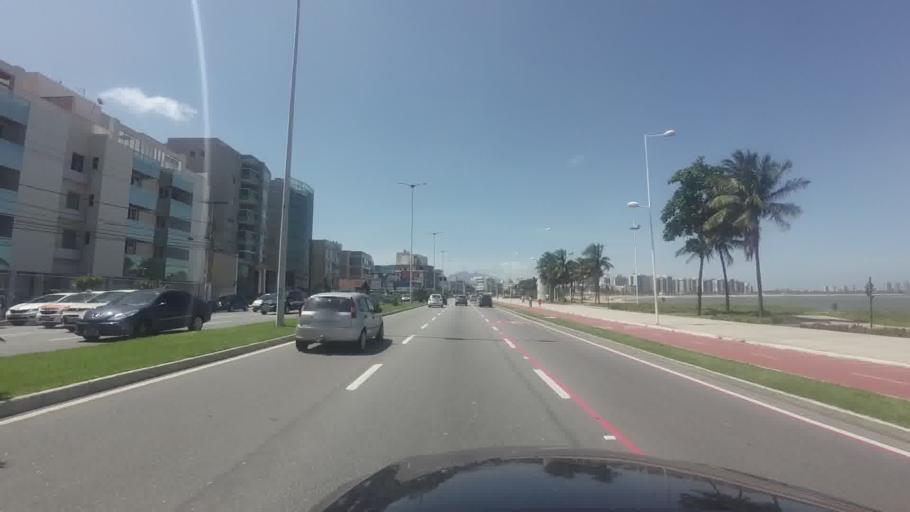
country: BR
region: Espirito Santo
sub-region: Vila Velha
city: Vila Velha
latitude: -20.2895
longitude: -40.2906
